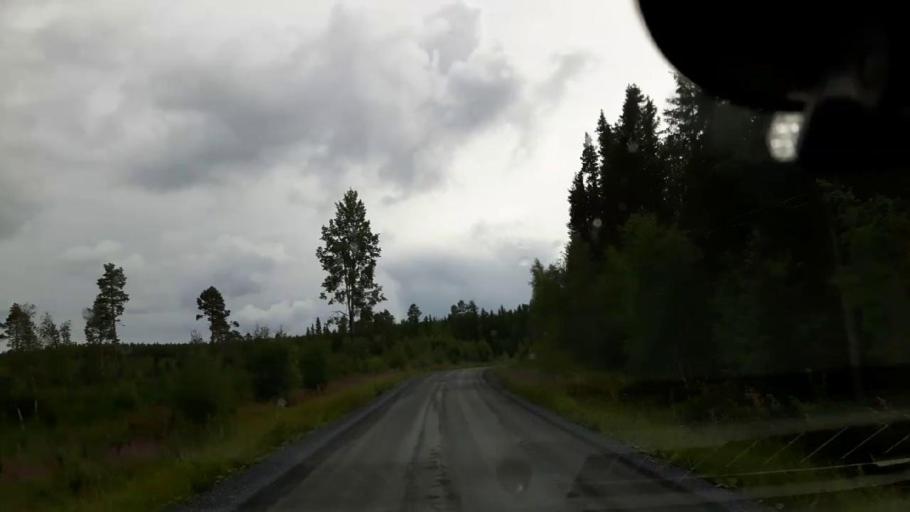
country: SE
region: Jaemtland
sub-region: Krokoms Kommun
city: Valla
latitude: 63.3722
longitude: 13.8827
